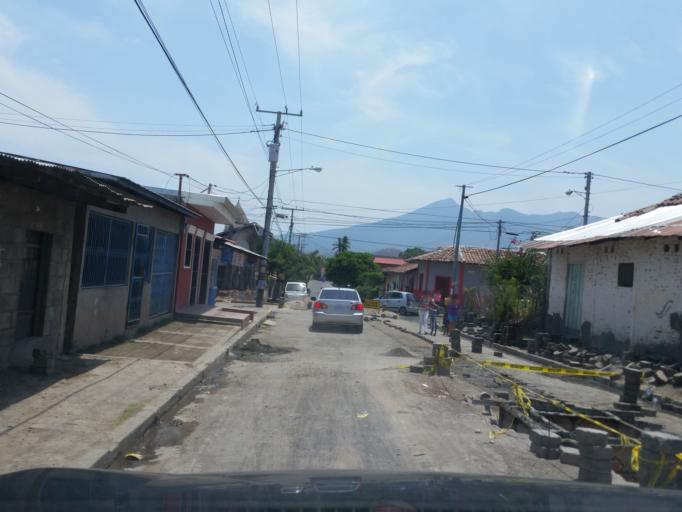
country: NI
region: Granada
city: Granada
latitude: 11.9324
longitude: -85.9480
